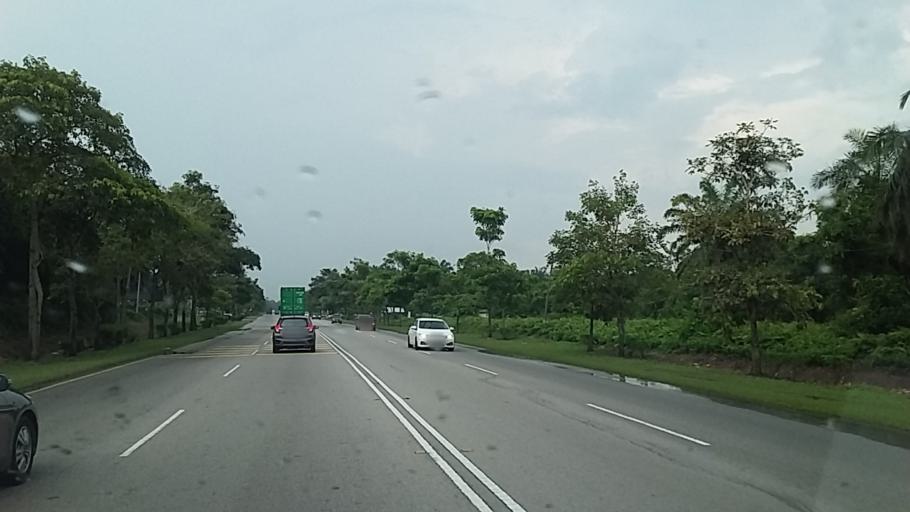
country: MY
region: Johor
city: Parit Raja
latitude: 1.8768
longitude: 103.1433
